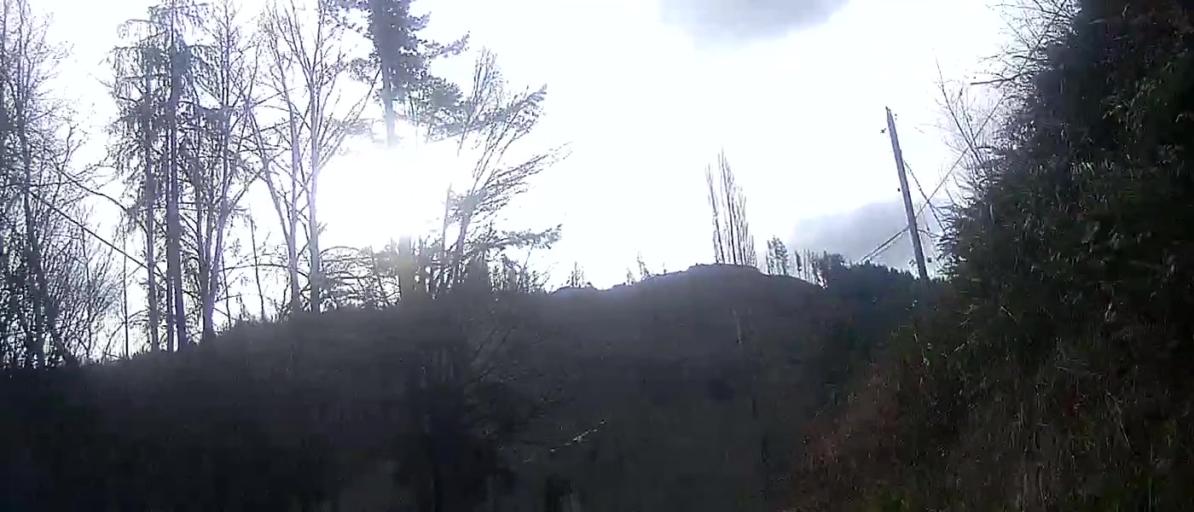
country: US
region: Washington
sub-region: Skagit County
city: Sedro-Woolley
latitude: 48.5564
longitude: -122.2905
